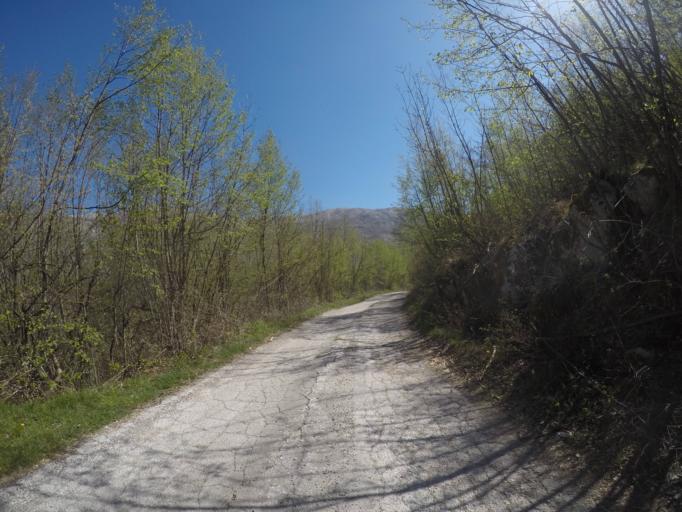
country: ME
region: Danilovgrad
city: Danilovgrad
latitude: 42.5412
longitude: 19.0018
